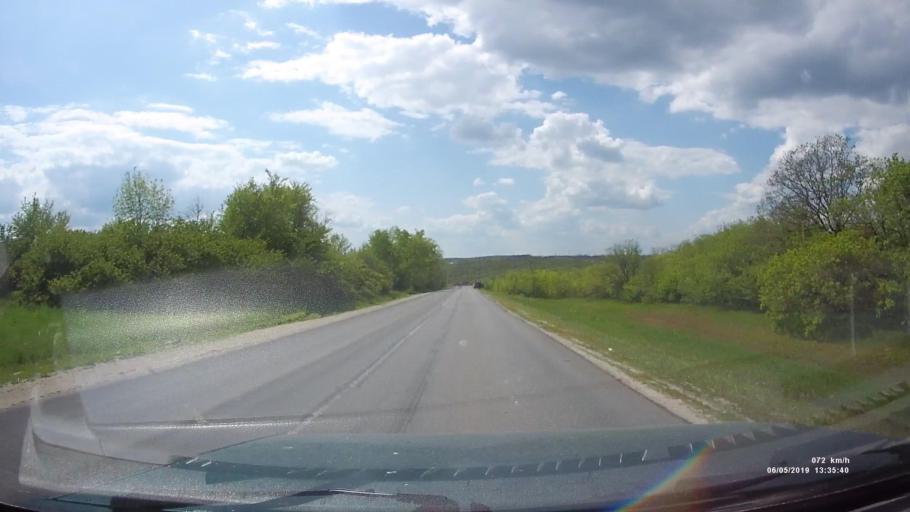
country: RU
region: Rostov
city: Ust'-Donetskiy
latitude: 47.6922
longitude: 40.7403
